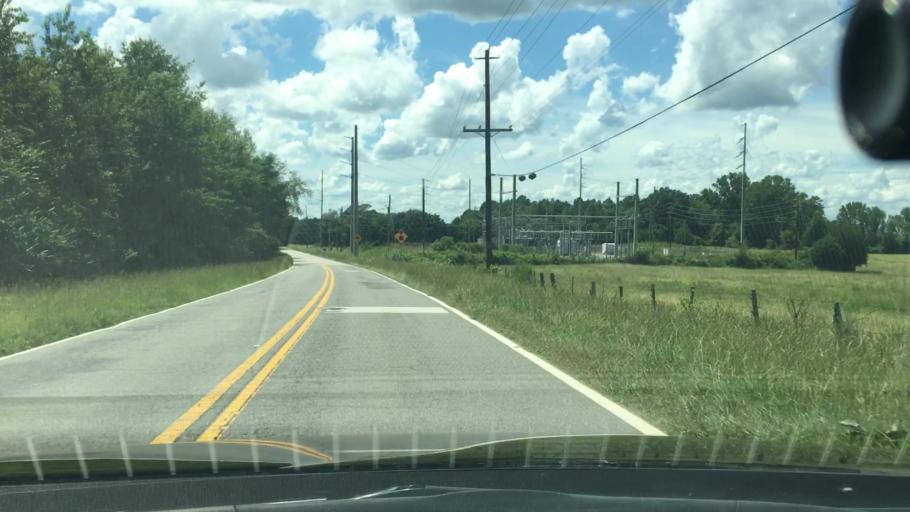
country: US
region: Georgia
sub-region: Putnam County
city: Jefferson
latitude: 33.3658
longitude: -83.2754
